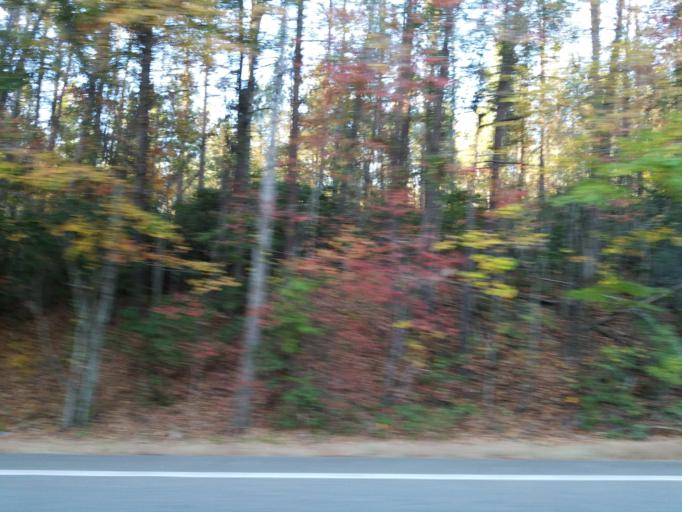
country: US
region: Georgia
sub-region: Dawson County
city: Dawsonville
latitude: 34.5483
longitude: -84.2285
